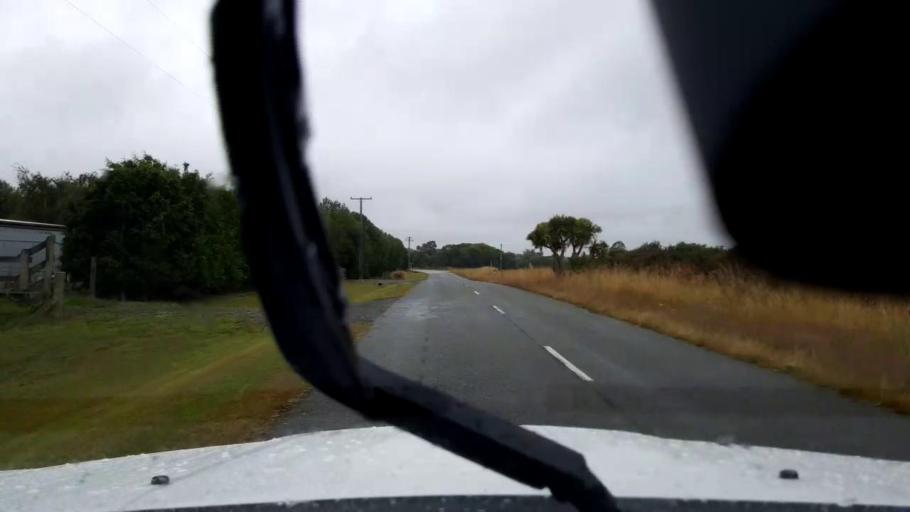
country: NZ
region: Canterbury
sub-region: Timaru District
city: Pleasant Point
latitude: -44.2532
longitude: 171.2509
